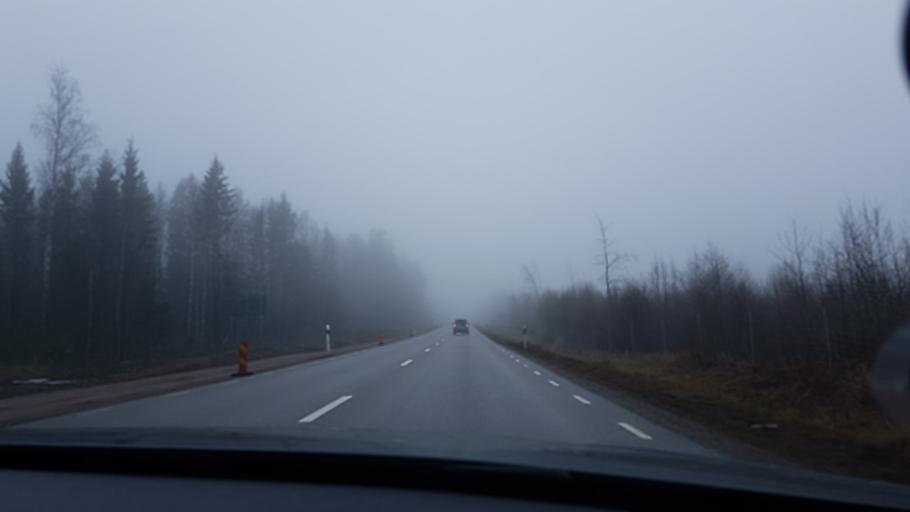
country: SE
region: Vaestra Goetaland
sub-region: Gullspangs Kommun
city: Gullspang
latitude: 58.9595
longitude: 14.0588
